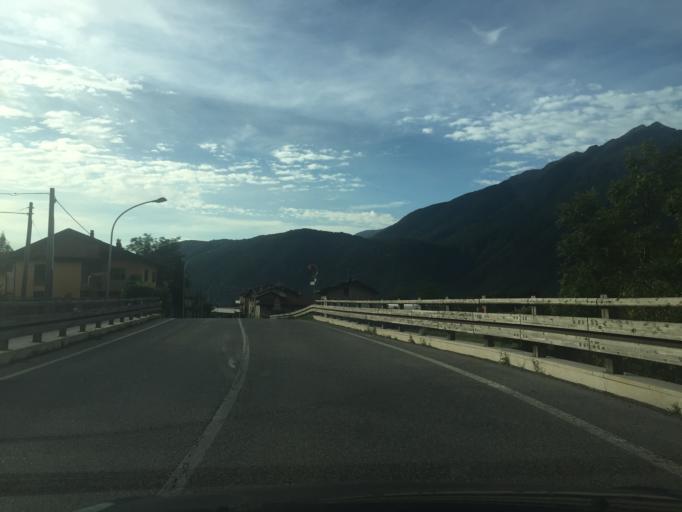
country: IT
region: Friuli Venezia Giulia
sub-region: Provincia di Udine
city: Villa Santina
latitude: 46.4196
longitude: 12.9113
